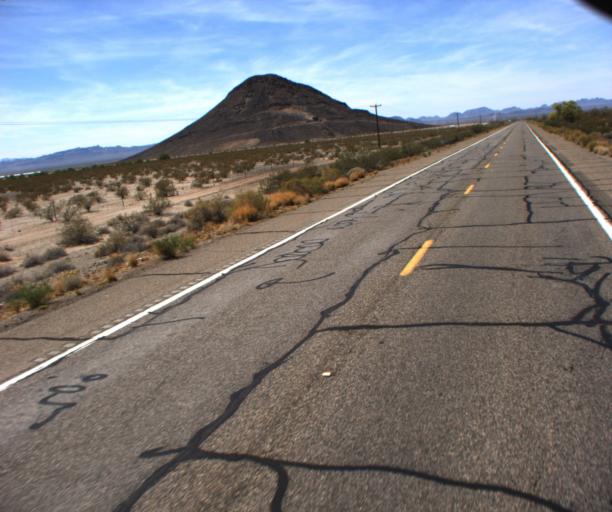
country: US
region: Arizona
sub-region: La Paz County
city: Salome
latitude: 33.7206
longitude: -113.7401
